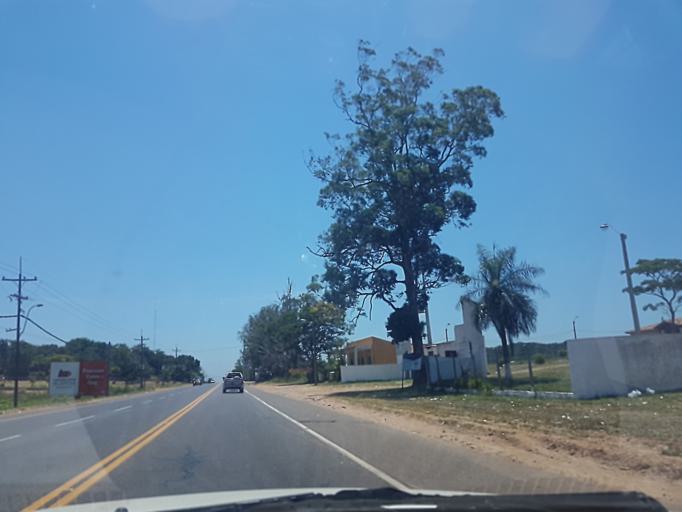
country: PY
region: Cordillera
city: Eusebio Ayala
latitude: -25.3837
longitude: -57.0501
